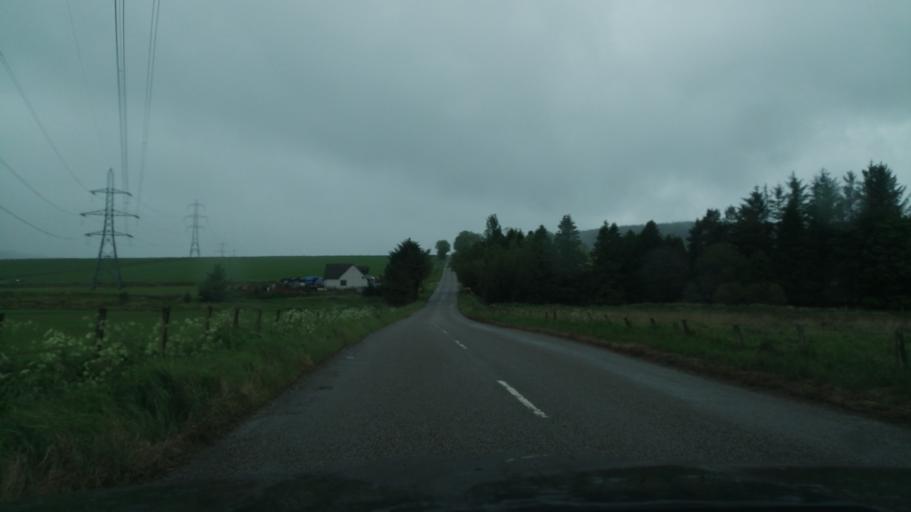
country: GB
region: Scotland
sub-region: Aberdeenshire
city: Huntly
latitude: 57.5446
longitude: -2.8067
